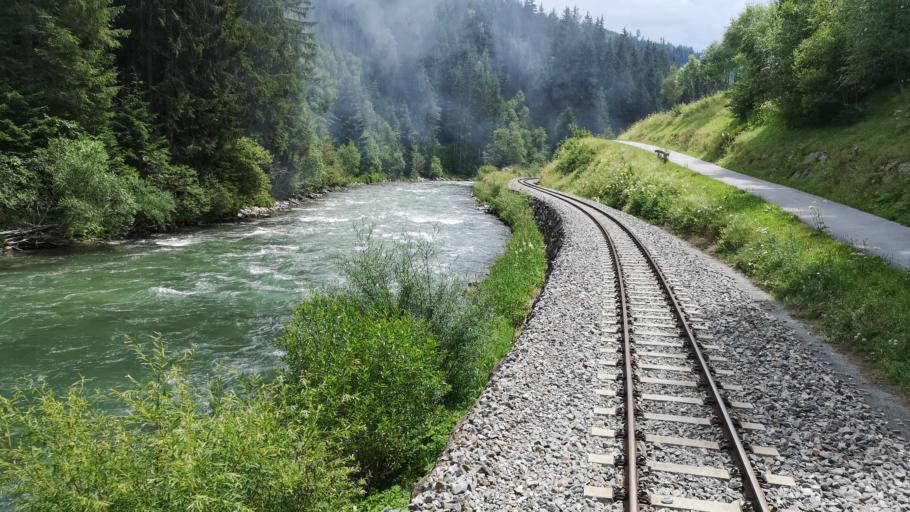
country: AT
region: Salzburg
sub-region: Politischer Bezirk Tamsweg
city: Tamsweg
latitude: 47.0970
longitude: 13.8207
